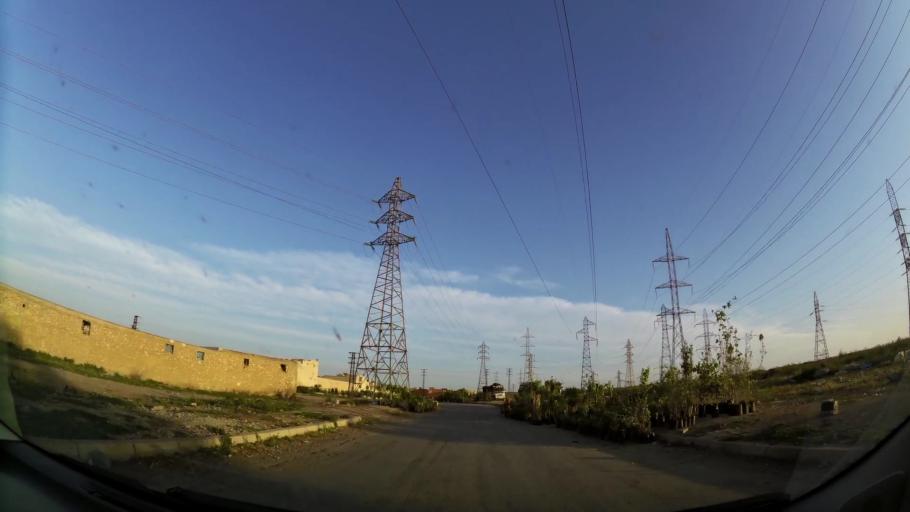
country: MA
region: Oriental
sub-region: Oujda-Angad
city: Oujda
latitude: 34.7104
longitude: -1.9161
